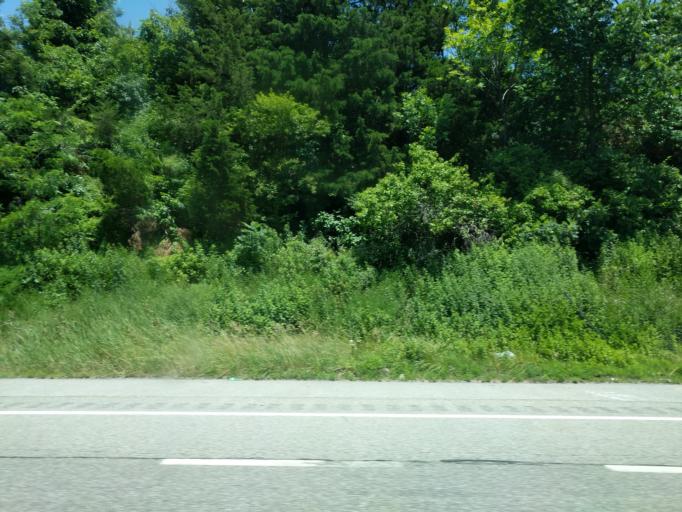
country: US
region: New York
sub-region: Orange County
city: Harriman
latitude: 41.3216
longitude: -74.1505
